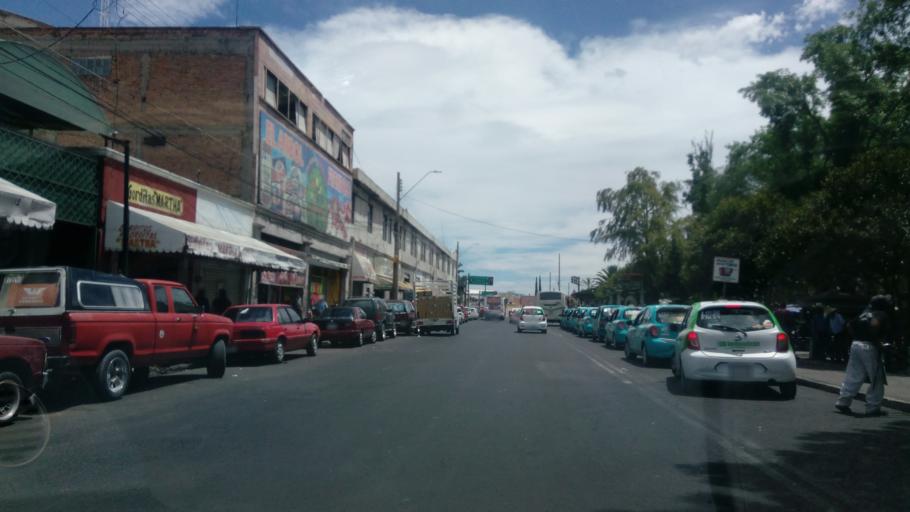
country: MX
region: Durango
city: Victoria de Durango
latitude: 24.0212
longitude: -104.6681
